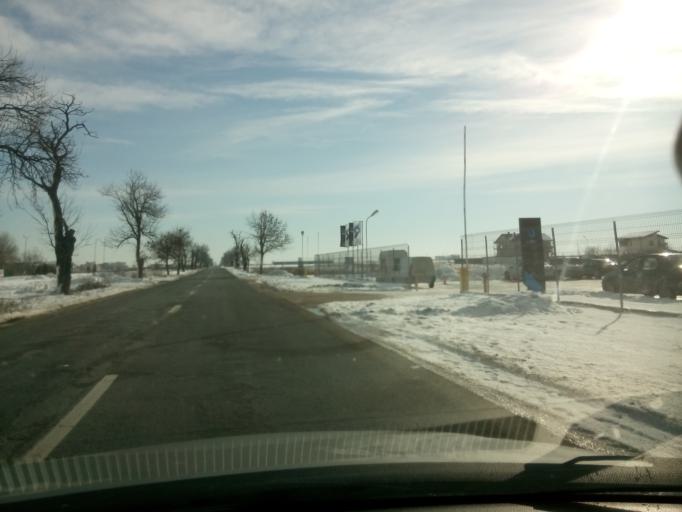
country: RO
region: Ilfov
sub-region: Comuna Glina
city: Glina
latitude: 44.3413
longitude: 26.2329
